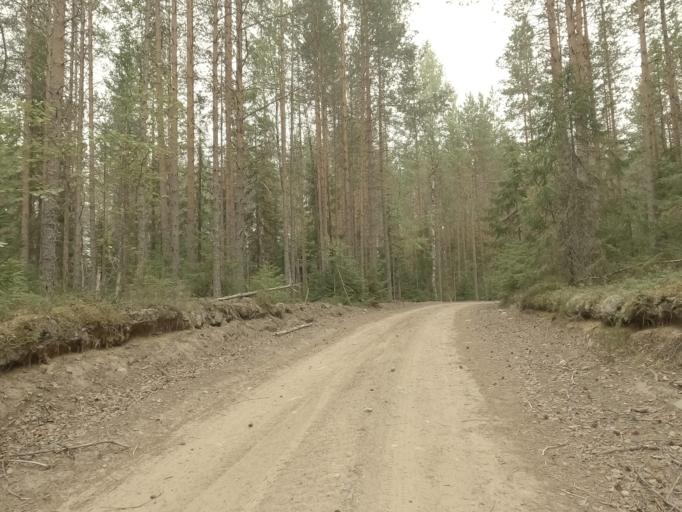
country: RU
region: Leningrad
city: Kamennogorsk
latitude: 61.0403
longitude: 29.1875
